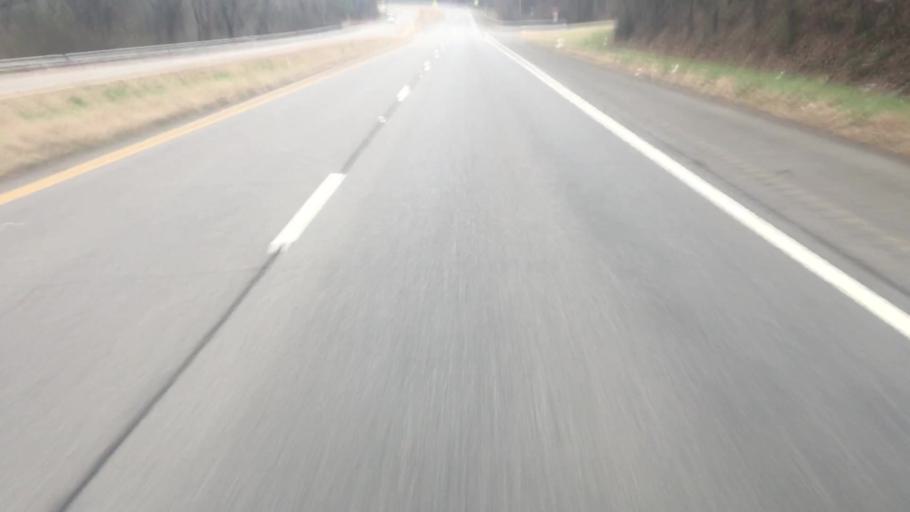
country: US
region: Alabama
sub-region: Walker County
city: Cordova
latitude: 33.8231
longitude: -87.1909
